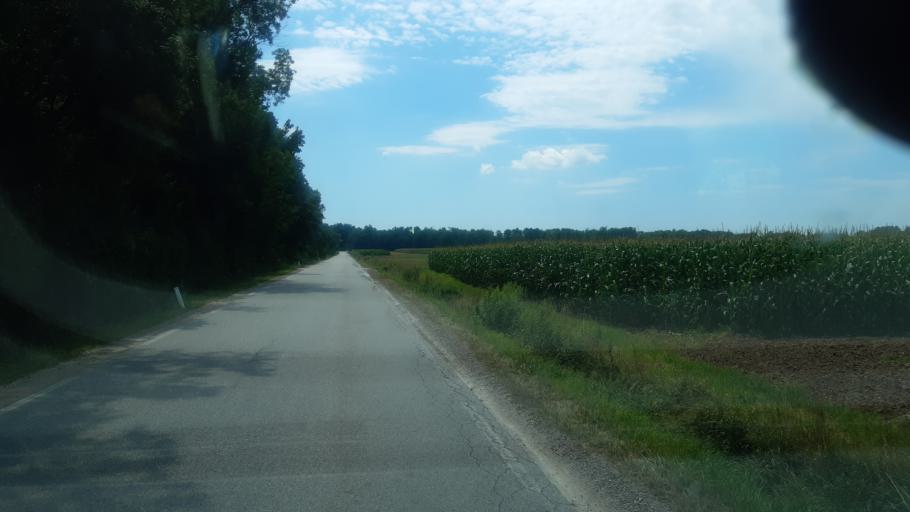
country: SI
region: Beltinci
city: Gancani
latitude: 46.6492
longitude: 16.2695
